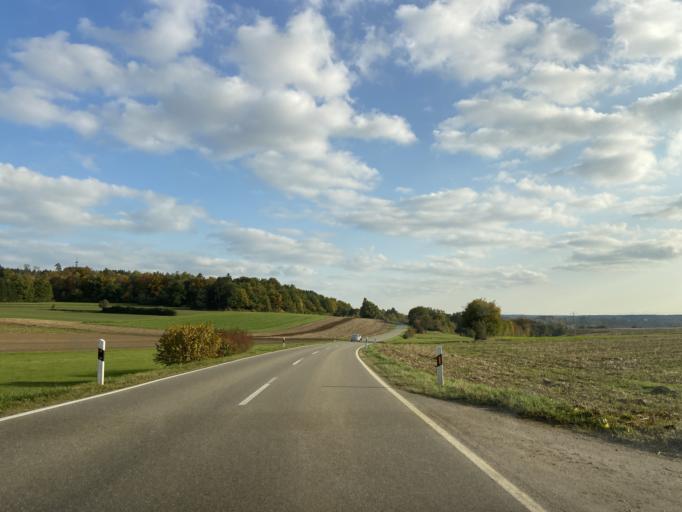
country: DE
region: Baden-Wuerttemberg
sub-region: Tuebingen Region
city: Scheer
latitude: 48.0864
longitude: 9.2884
